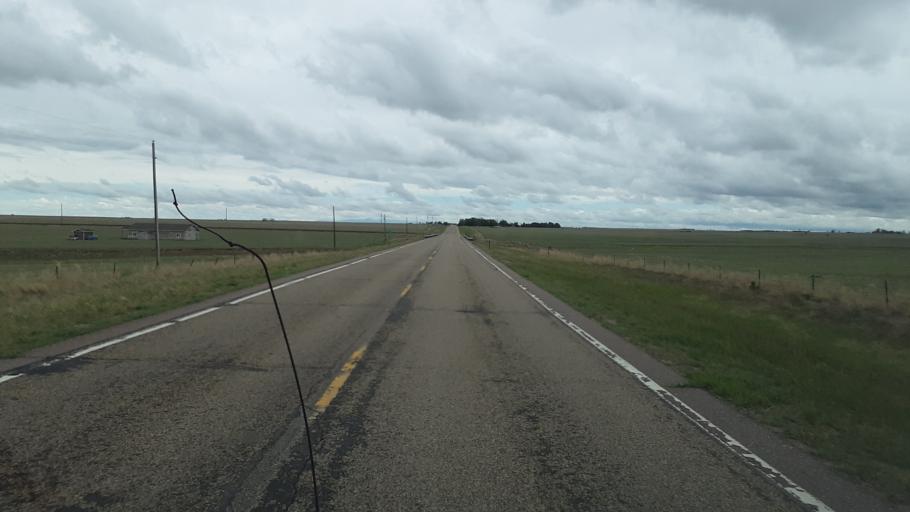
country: US
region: Colorado
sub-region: El Paso County
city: Ellicott
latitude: 38.8399
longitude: -104.0356
